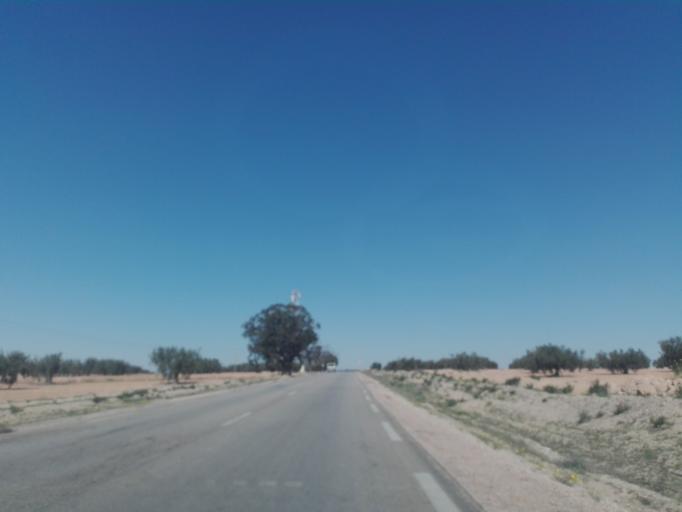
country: TN
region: Safaqis
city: Bi'r `Ali Bin Khalifah
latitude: 34.7552
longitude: 10.3323
